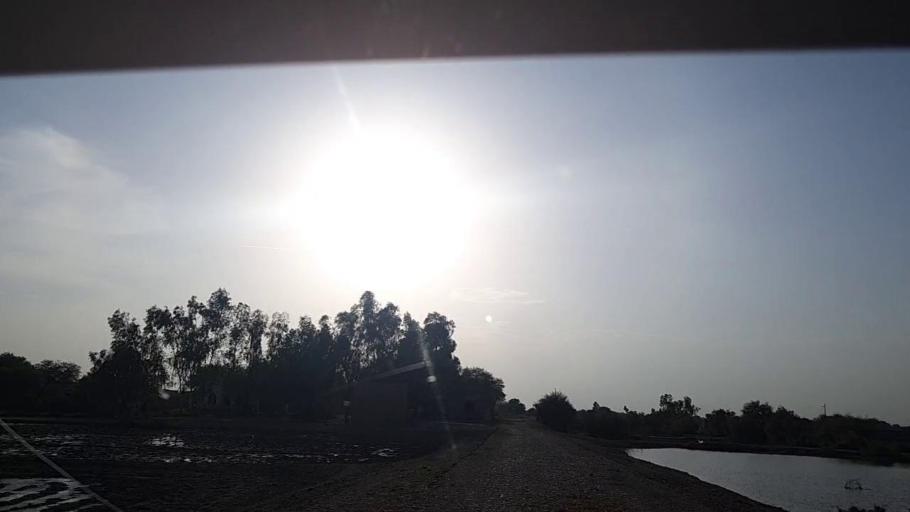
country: PK
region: Sindh
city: Khanpur
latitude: 27.8070
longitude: 69.3312
